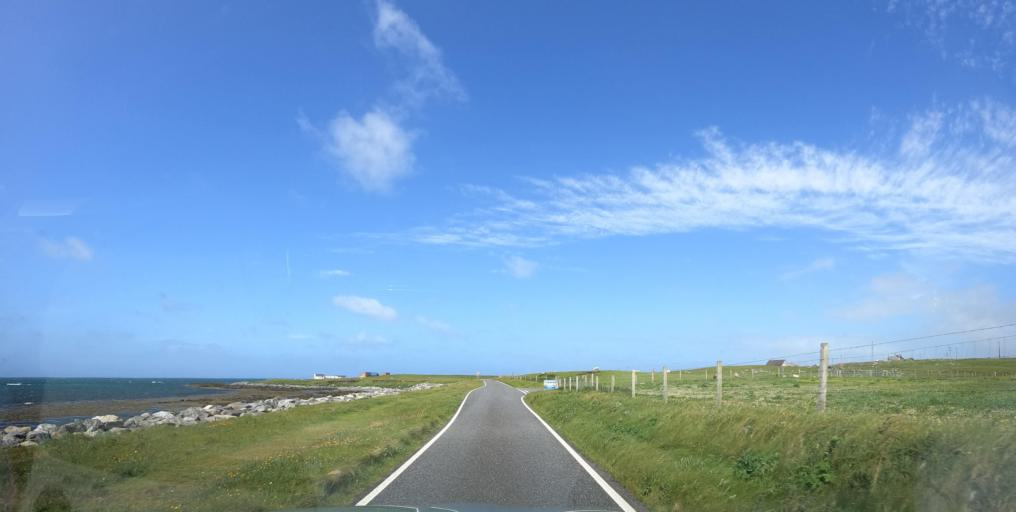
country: GB
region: Scotland
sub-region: Eilean Siar
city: Isle of South Uist
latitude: 57.1041
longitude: -7.3635
